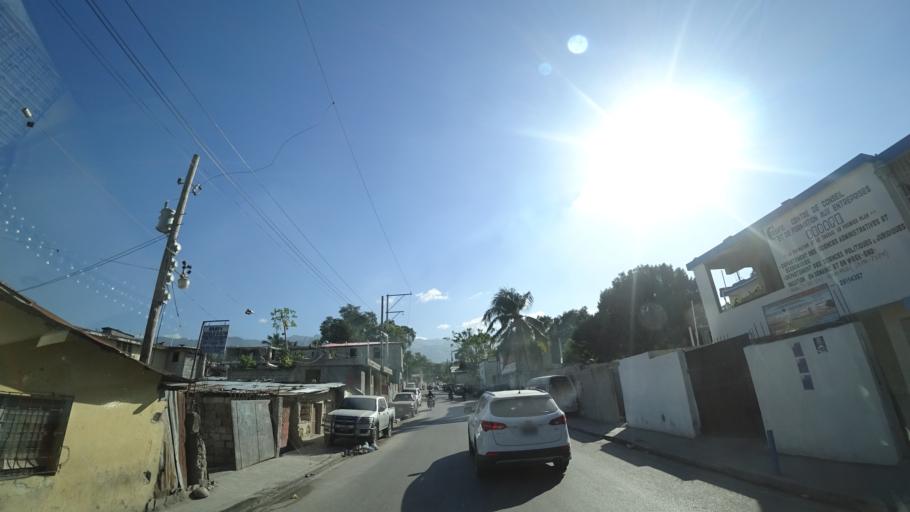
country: HT
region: Ouest
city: Petionville
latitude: 18.5257
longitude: -72.2825
